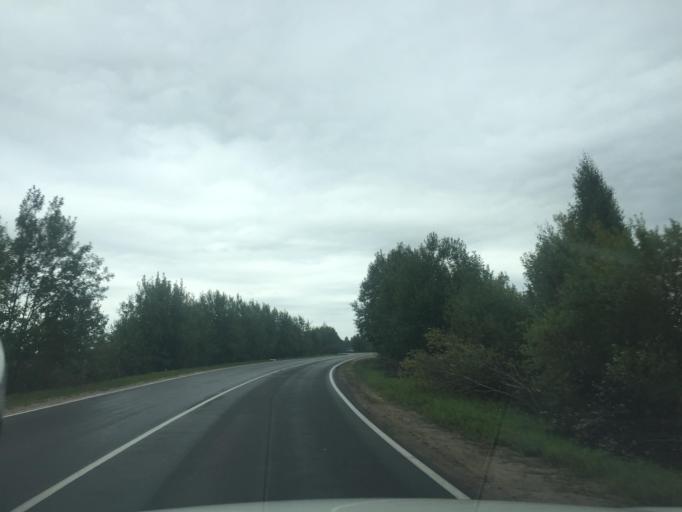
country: RU
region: Leningrad
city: Siverskiy
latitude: 59.3320
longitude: 30.0299
